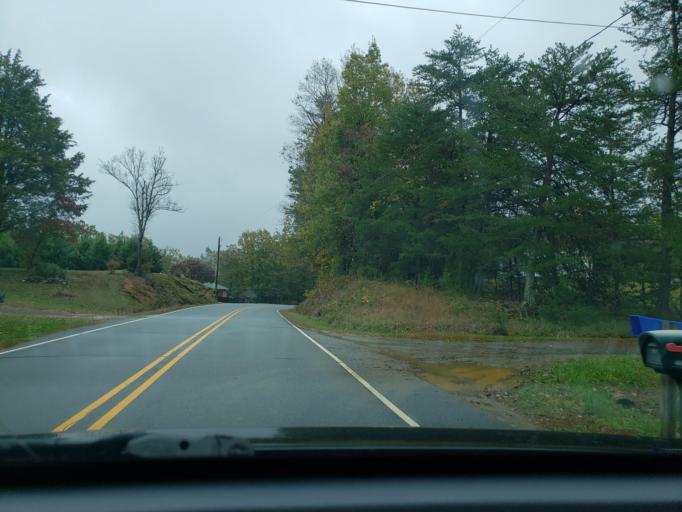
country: US
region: North Carolina
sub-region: Stokes County
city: Danbury
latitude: 36.4153
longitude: -80.2435
